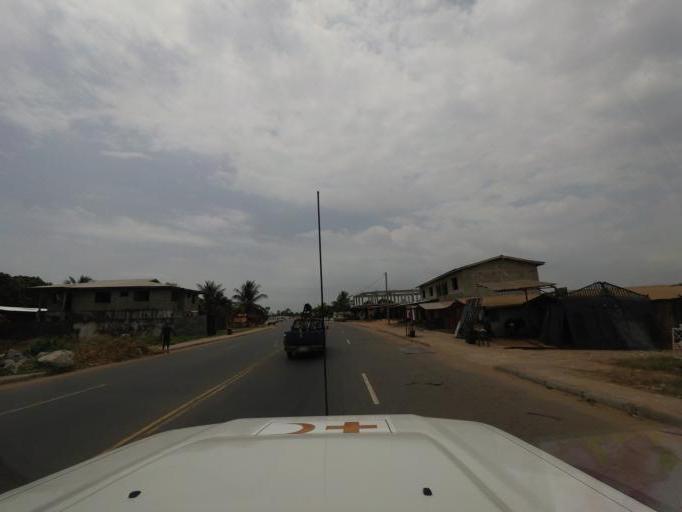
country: LR
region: Montserrado
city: Monrovia
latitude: 6.2856
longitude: -10.7158
